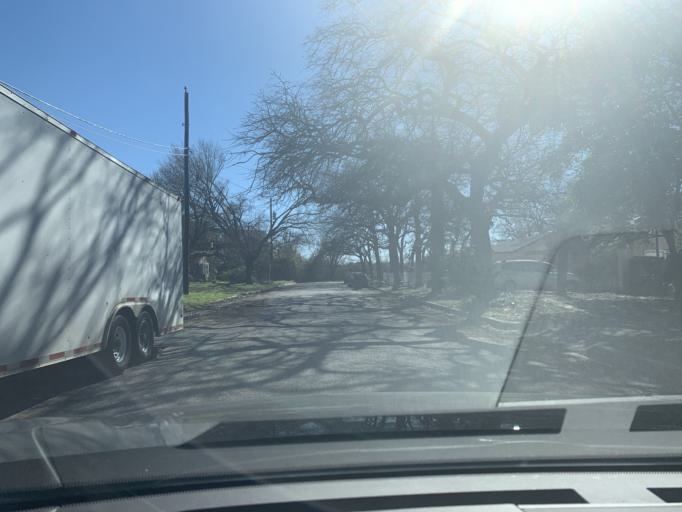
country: US
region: Texas
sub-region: Tarrant County
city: Haltom City
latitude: 32.7722
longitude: -97.2898
